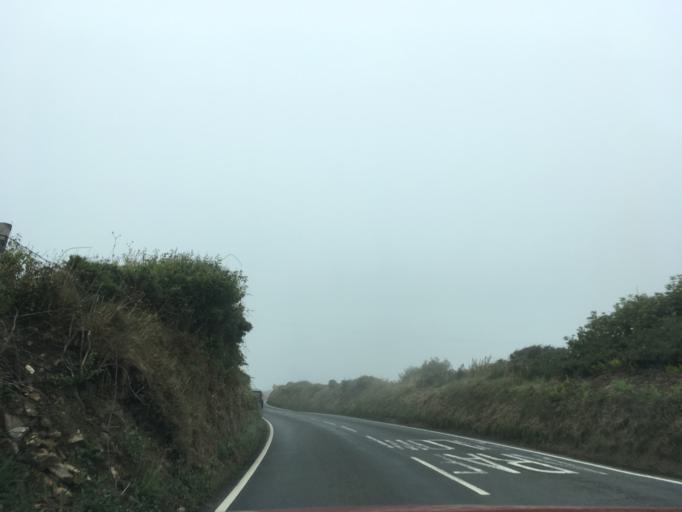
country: GB
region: Wales
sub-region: Pembrokeshire
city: Llanrhian
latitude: 51.8621
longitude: -5.1231
